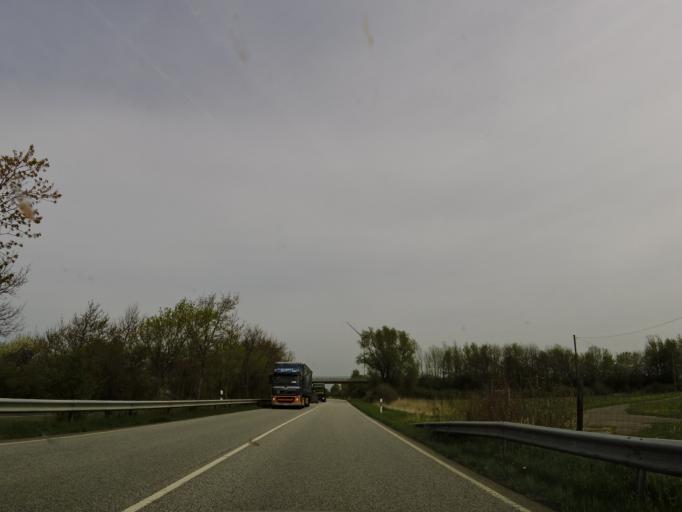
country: DE
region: Schleswig-Holstein
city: Stelle-Wittenwurth
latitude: 54.2414
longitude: 9.0374
